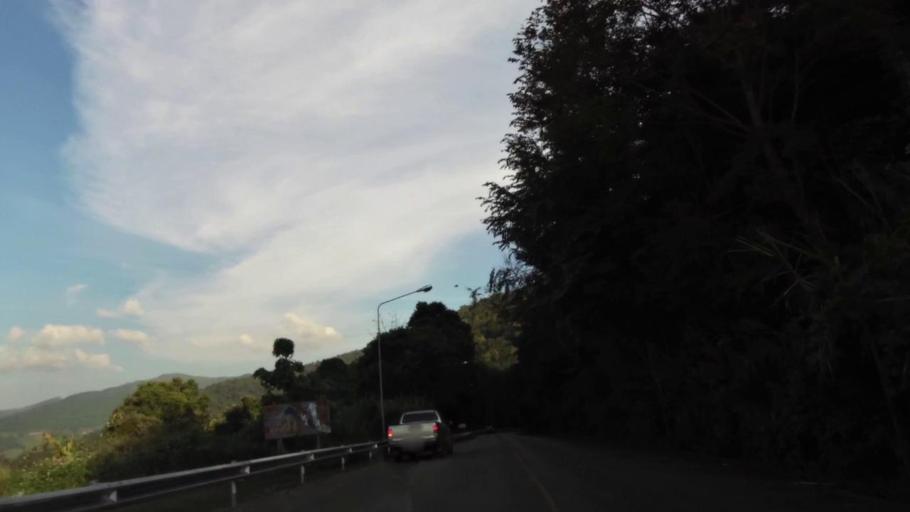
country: TH
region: Chiang Rai
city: Khun Tan
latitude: 19.8660
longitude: 100.4417
